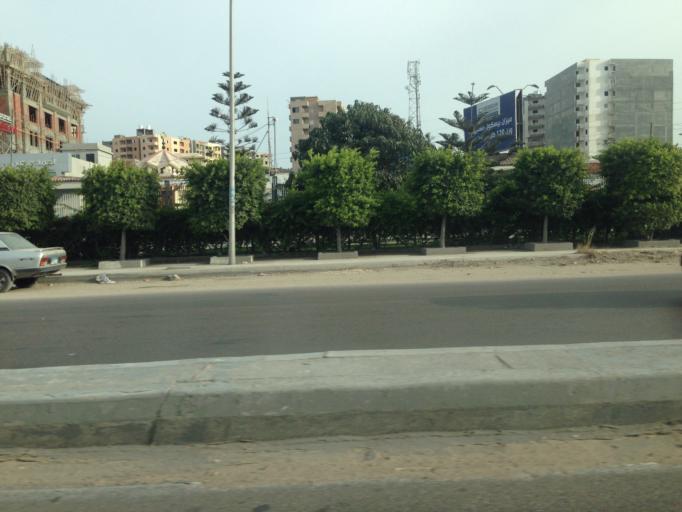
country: EG
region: Alexandria
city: Alexandria
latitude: 31.2039
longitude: 29.9817
